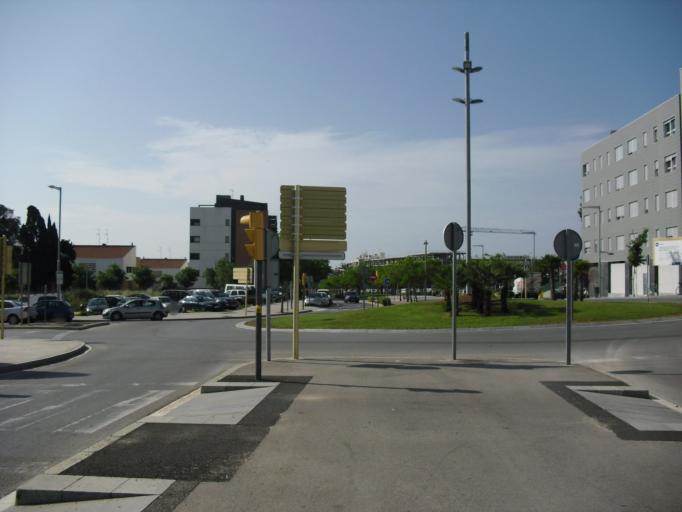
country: ES
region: Catalonia
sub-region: Provincia de Barcelona
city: Vilanova i la Geltru
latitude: 41.2310
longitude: 1.7296
